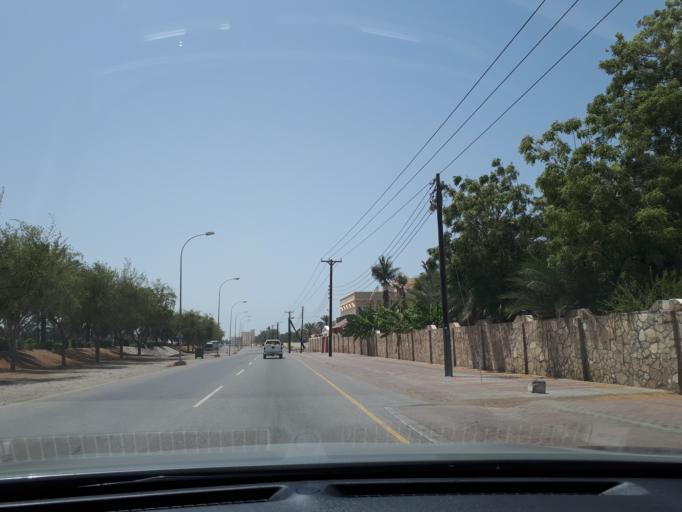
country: OM
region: Muhafazat Masqat
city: As Sib al Jadidah
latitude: 23.6928
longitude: 58.0735
